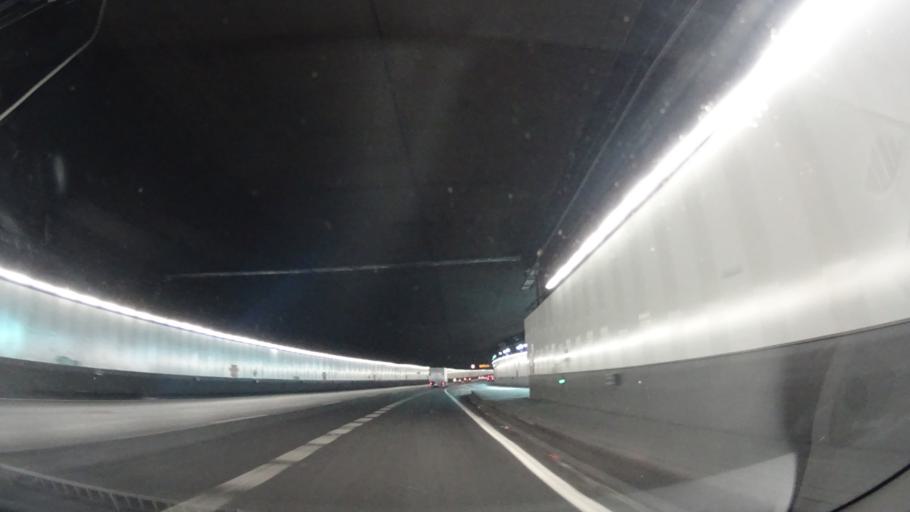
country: ES
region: Madrid
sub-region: Provincia de Madrid
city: Usera
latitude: 40.3941
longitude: -3.7039
